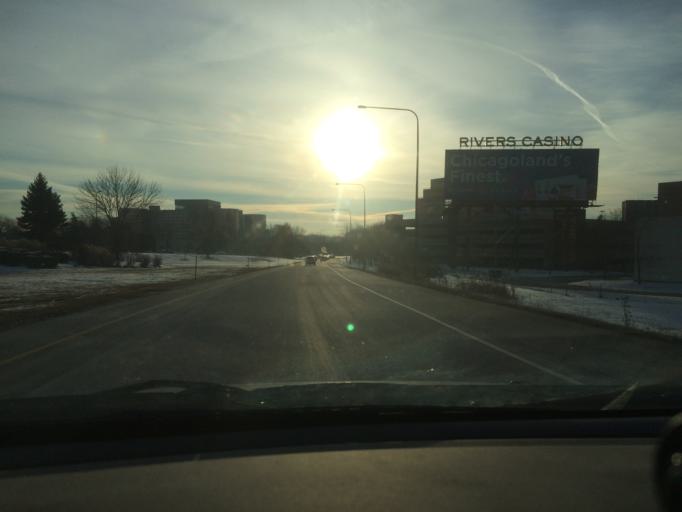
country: US
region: Illinois
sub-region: Cook County
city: Rosemont
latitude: 41.9830
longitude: -87.8652
